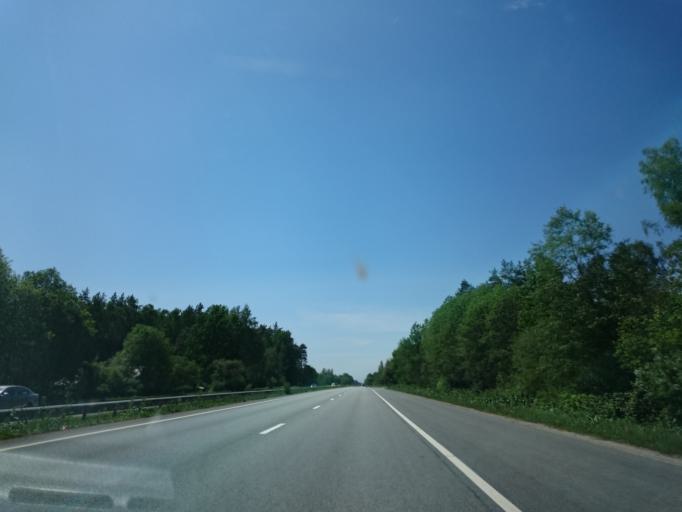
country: LV
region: Olaine
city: Olaine
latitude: 56.7567
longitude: 23.9024
